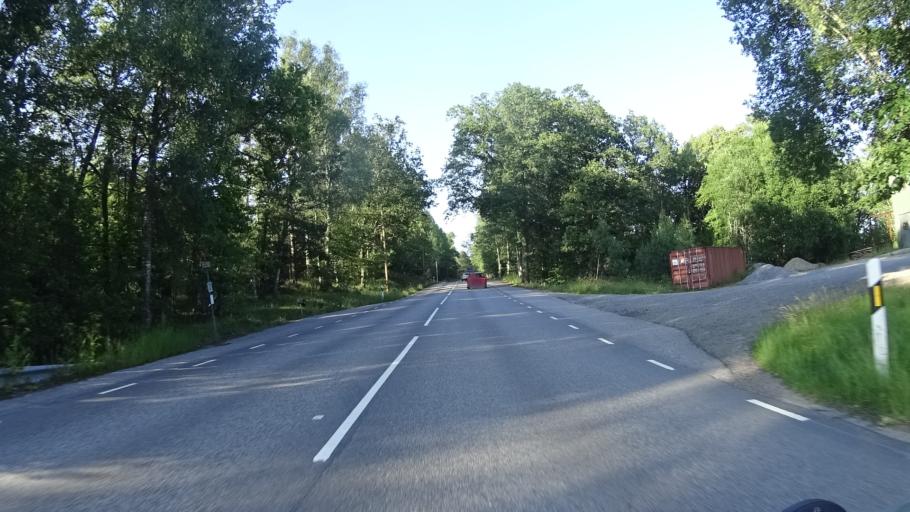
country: SE
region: Stockholm
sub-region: Sodertalje Kommun
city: Pershagen
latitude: 59.1169
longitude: 17.6402
